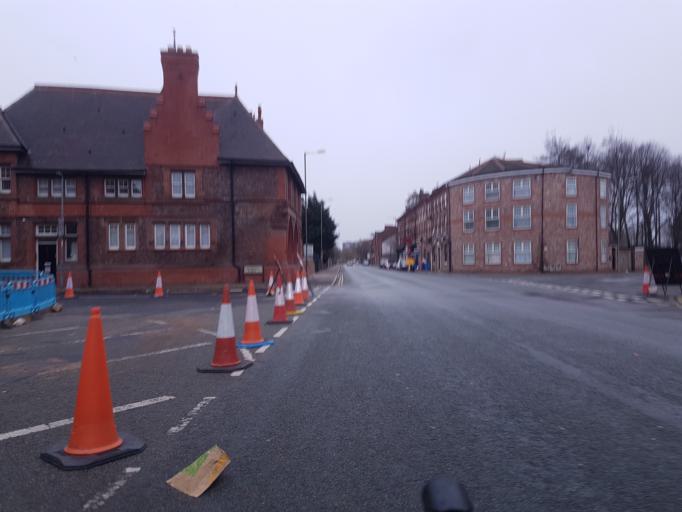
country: GB
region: England
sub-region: Liverpool
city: Liverpool
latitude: 53.4361
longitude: -2.9752
